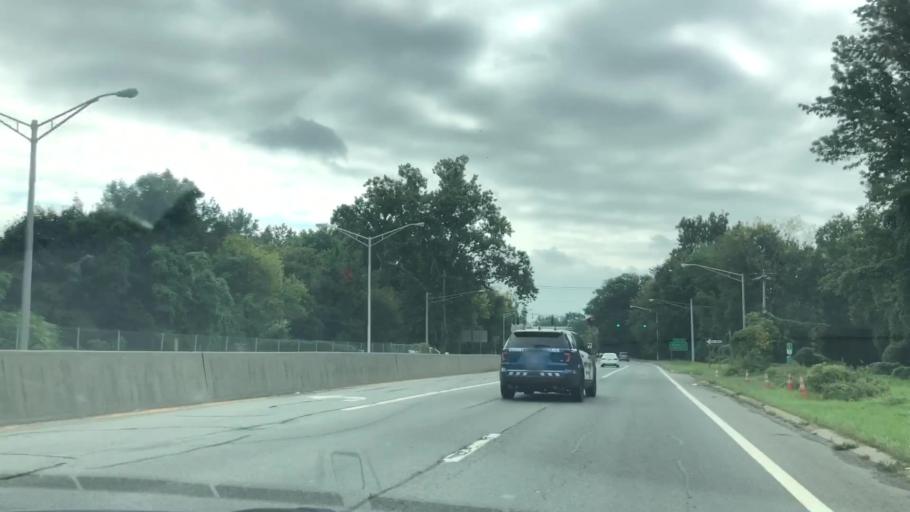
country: US
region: New York
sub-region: Westchester County
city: Hastings-on-Hudson
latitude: 40.9798
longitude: -73.8679
